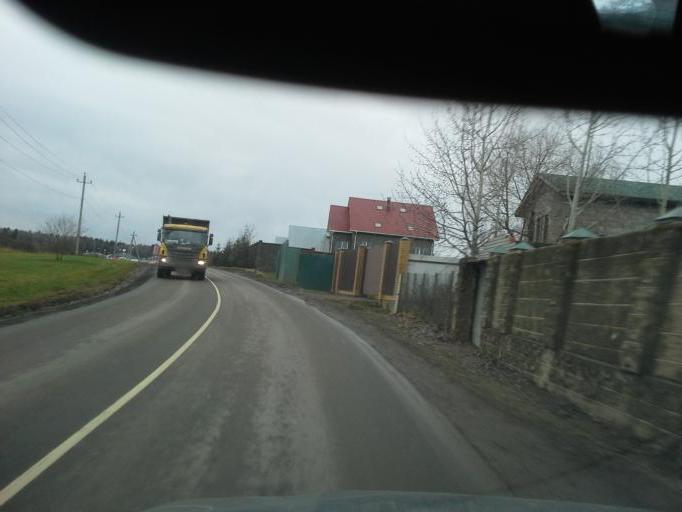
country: RU
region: Moskovskaya
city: Moskovskiy
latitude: 55.5721
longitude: 37.3861
